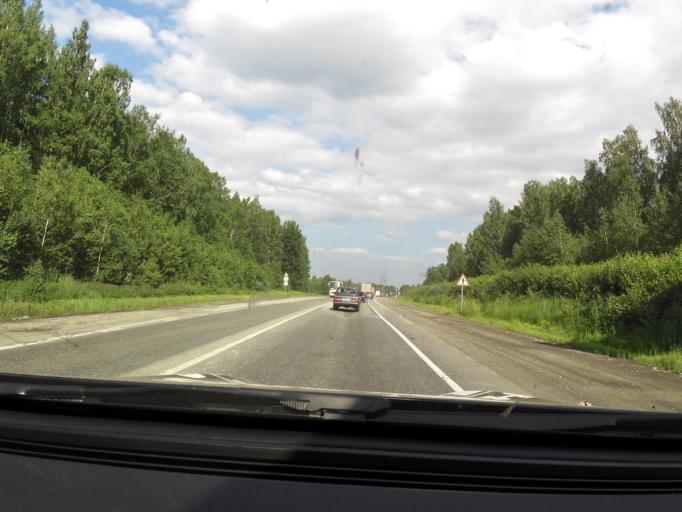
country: RU
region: Sverdlovsk
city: Talitsa
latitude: 56.8492
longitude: 60.0535
